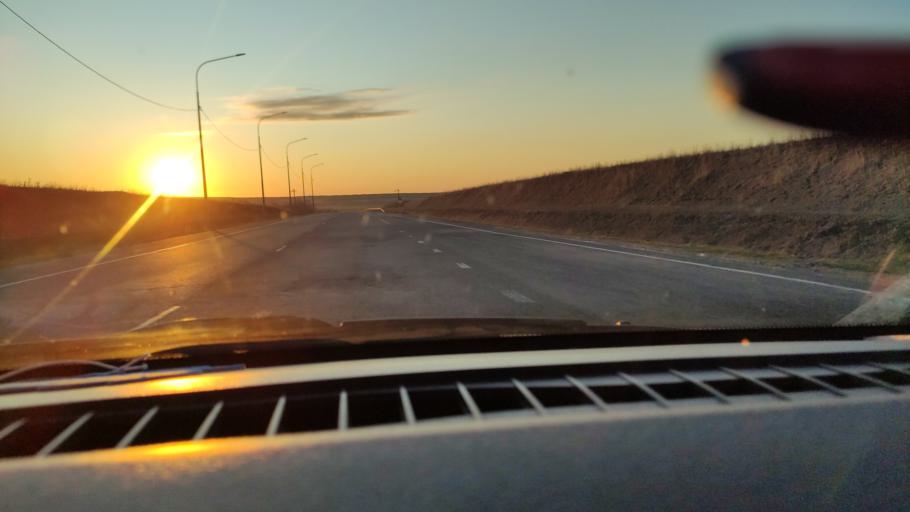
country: RU
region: Saratov
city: Yelshanka
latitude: 51.8310
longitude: 46.4419
